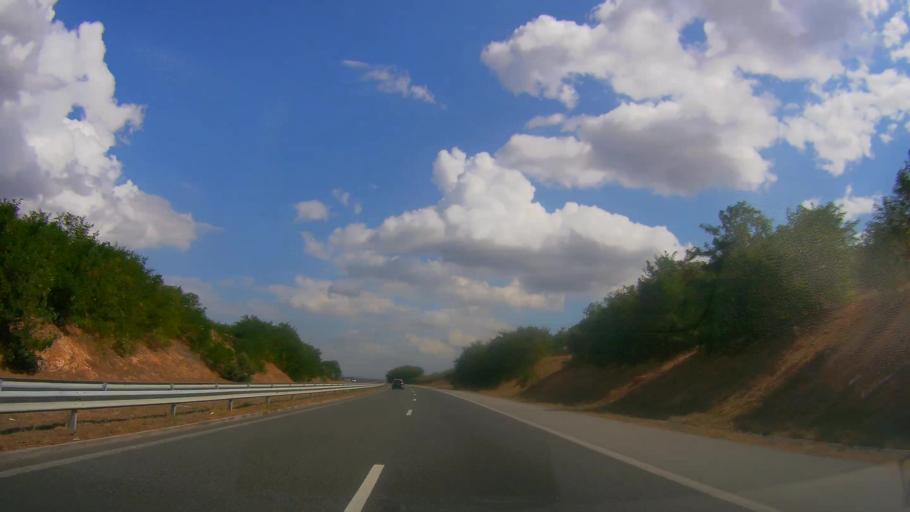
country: BG
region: Yambol
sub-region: Obshtina Yambol
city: Yambol
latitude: 42.5403
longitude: 26.4688
